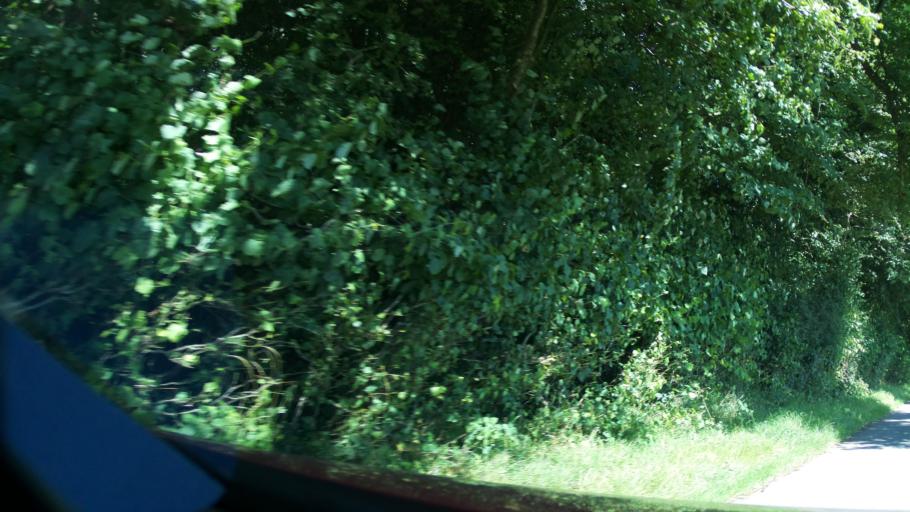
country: GB
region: England
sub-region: West Berkshire
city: Farnborough
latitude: 51.5105
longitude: -1.3983
